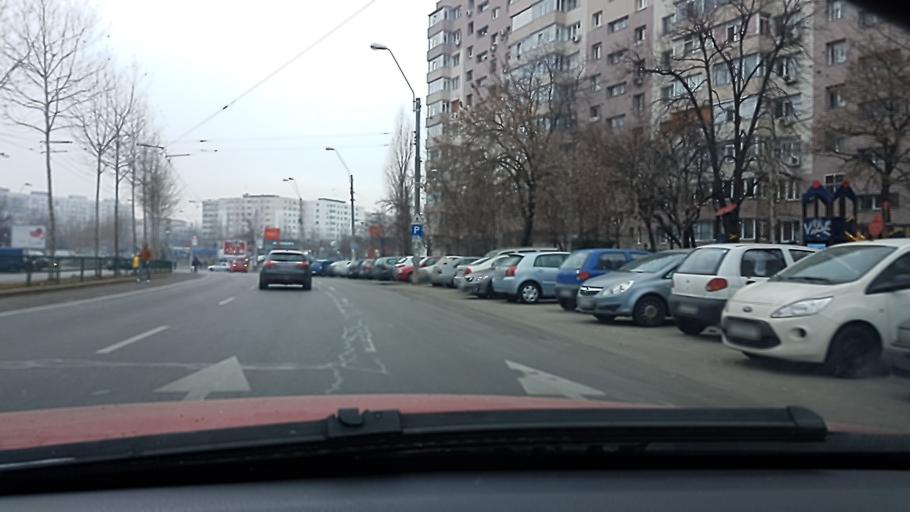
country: RO
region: Ilfov
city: Dobroesti
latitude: 44.4183
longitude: 26.1763
